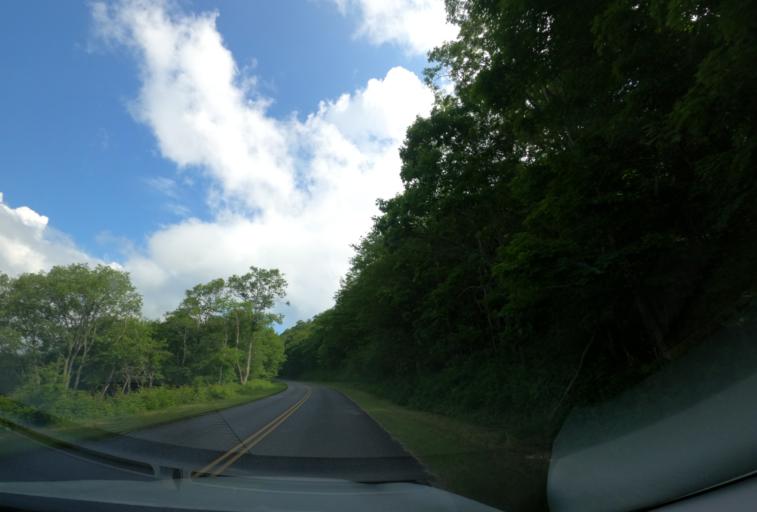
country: US
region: North Carolina
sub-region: Haywood County
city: Hazelwood
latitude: 35.4042
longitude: -83.0450
